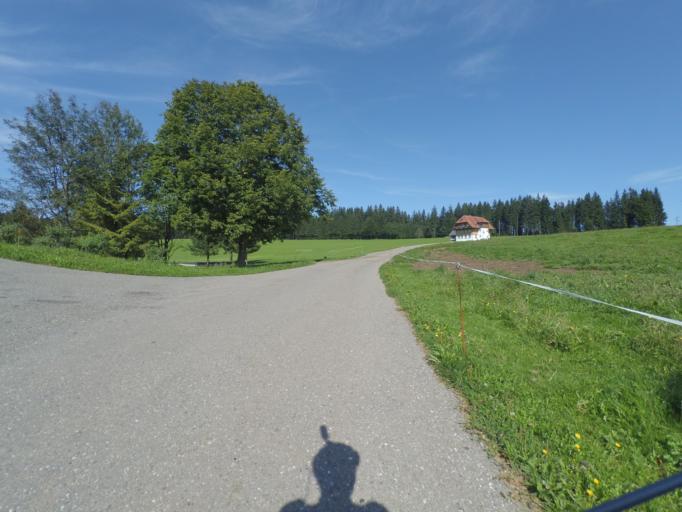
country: DE
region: Baden-Wuerttemberg
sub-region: Freiburg Region
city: Breitnau
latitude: 47.9644
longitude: 8.1233
